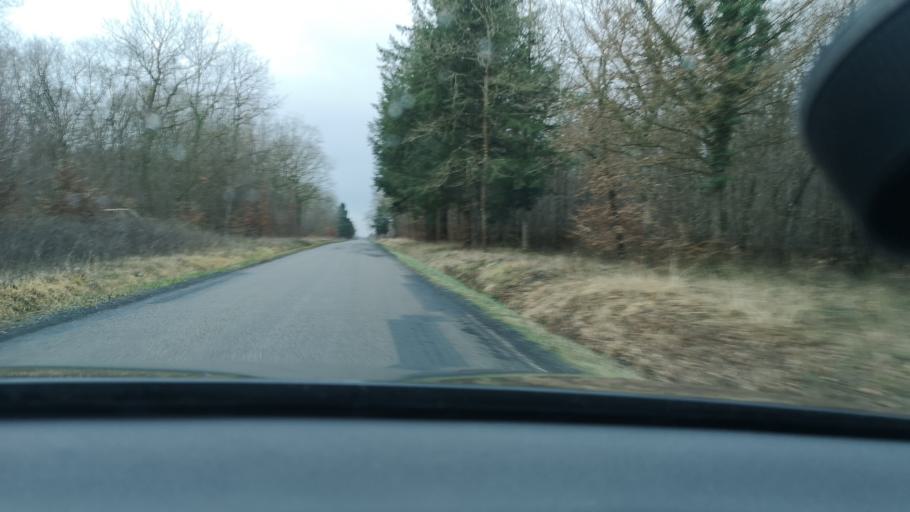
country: FR
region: Bourgogne
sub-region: Departement de Saone-et-Loire
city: Dracy-le-Fort
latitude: 46.7656
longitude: 4.7718
